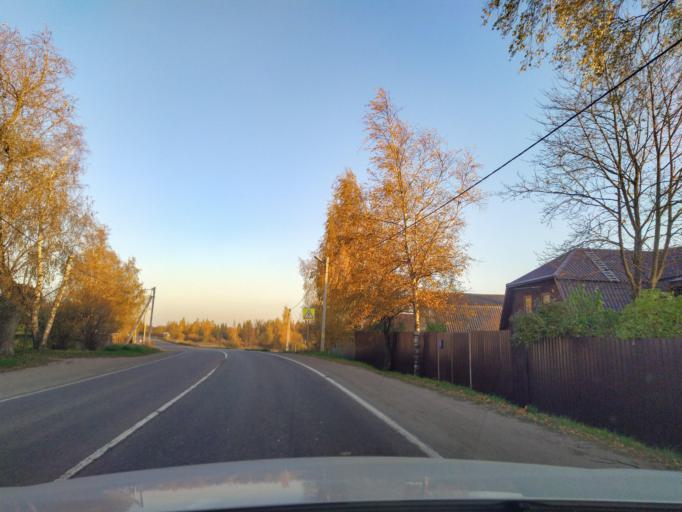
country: RU
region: Leningrad
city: Maloye Verevo
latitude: 59.6128
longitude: 30.2223
